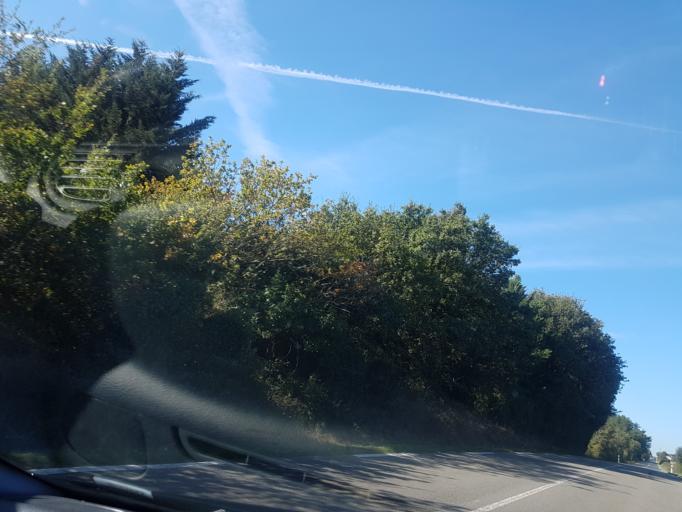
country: FR
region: Pays de la Loire
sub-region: Departement de la Loire-Atlantique
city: Casson
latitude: 47.4284
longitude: -1.5709
